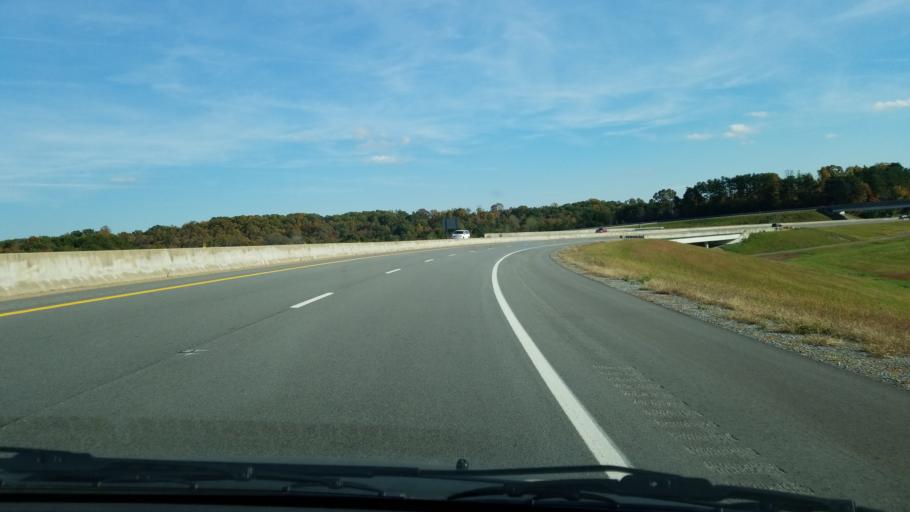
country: US
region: Tennessee
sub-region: Hamilton County
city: Soddy-Daisy
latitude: 35.3031
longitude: -85.1525
